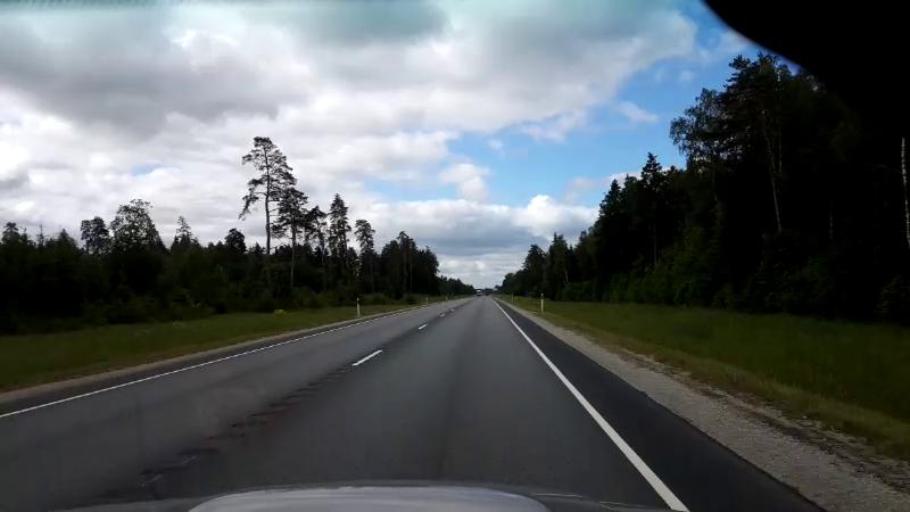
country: EE
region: Harju
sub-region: Nissi vald
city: Riisipere
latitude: 59.0924
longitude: 24.4645
